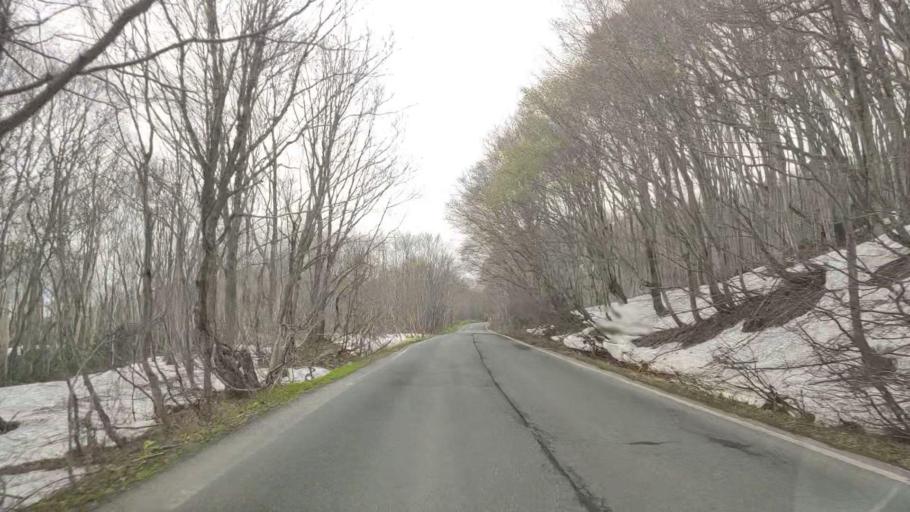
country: JP
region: Aomori
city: Aomori Shi
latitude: 40.6811
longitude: 140.9340
